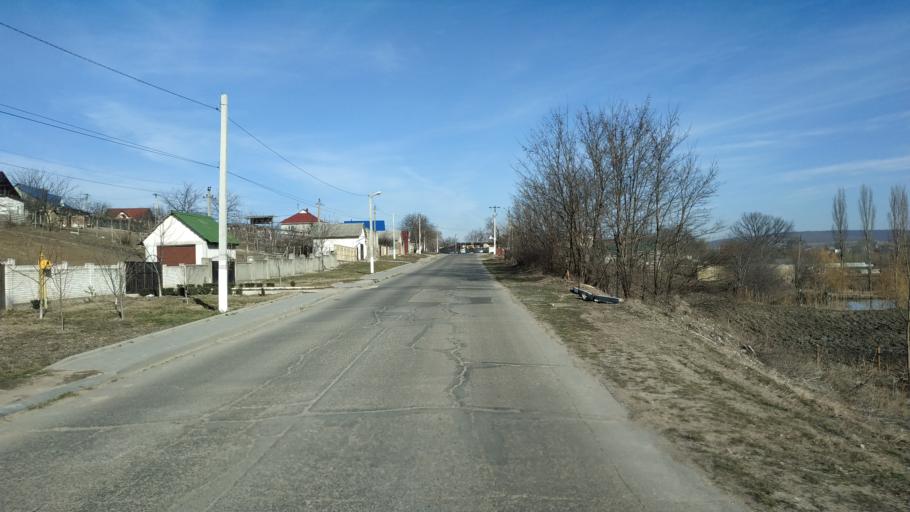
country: MD
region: Chisinau
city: Vatra
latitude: 47.0020
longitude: 28.6722
